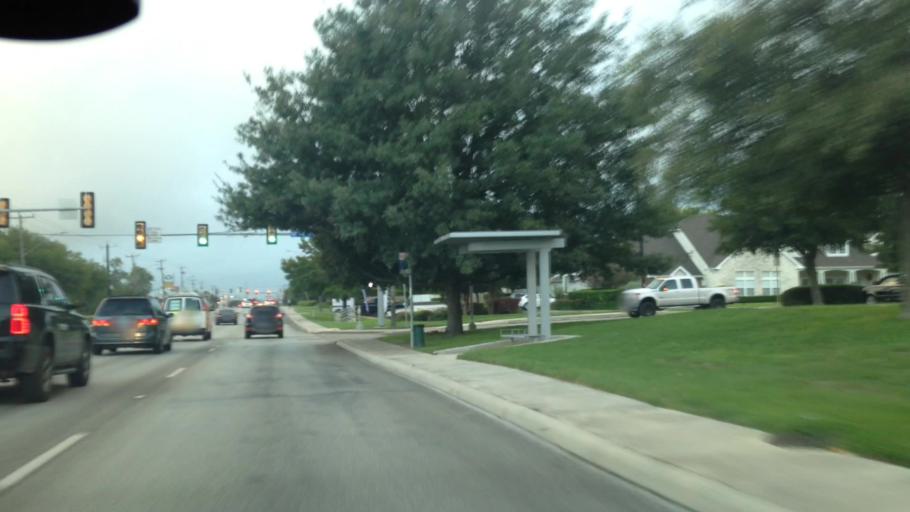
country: US
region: Texas
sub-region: Bexar County
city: Live Oak
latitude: 29.5739
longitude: -98.3780
